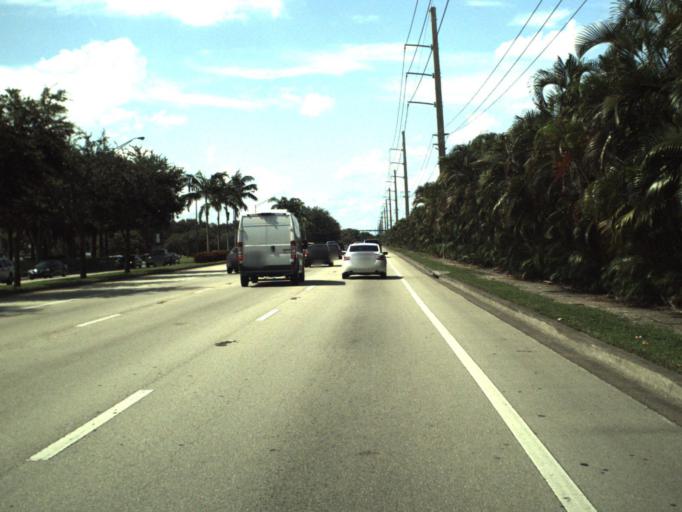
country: US
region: Florida
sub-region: Broward County
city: Pine Island Ridge
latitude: 26.1073
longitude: -80.2500
